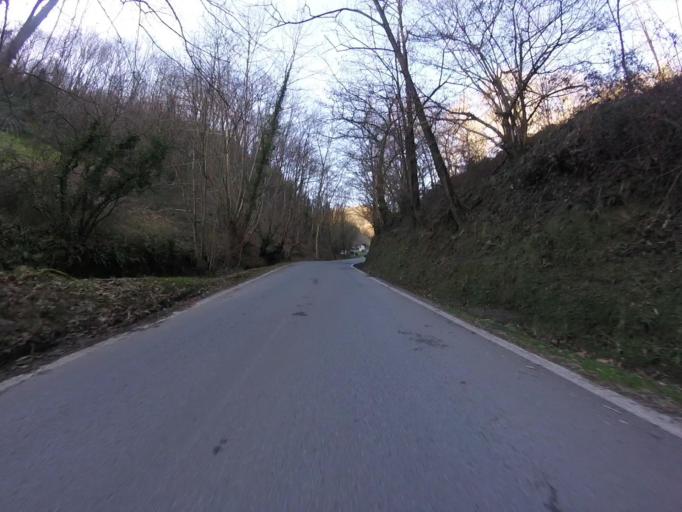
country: ES
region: Navarre
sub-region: Provincia de Navarra
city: Lesaka
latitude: 43.2525
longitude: -1.7224
